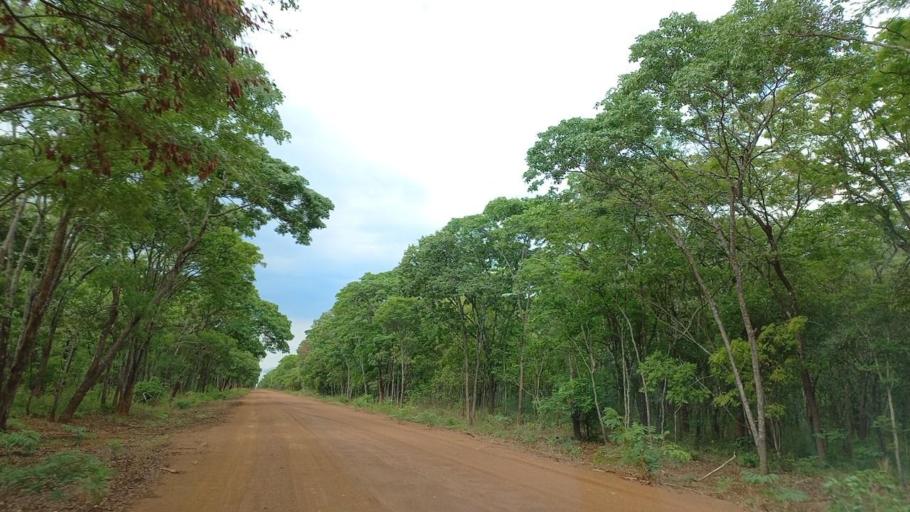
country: ZM
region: North-Western
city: Kalengwa
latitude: -13.4179
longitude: 25.0574
